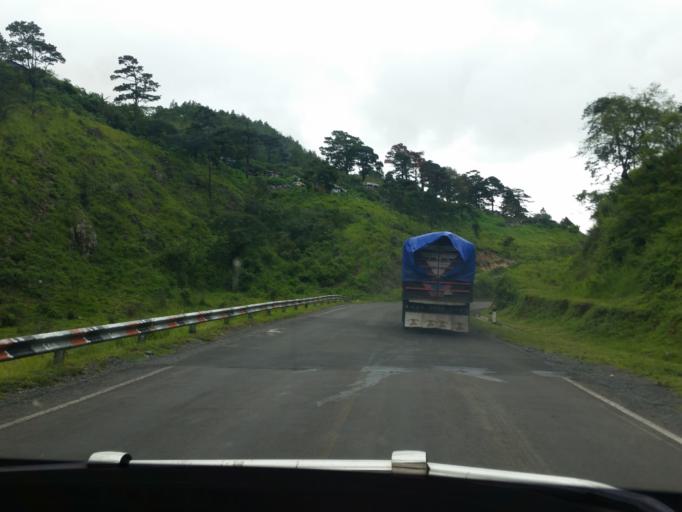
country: NI
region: Jinotega
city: Jinotega
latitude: 13.0478
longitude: -86.0002
